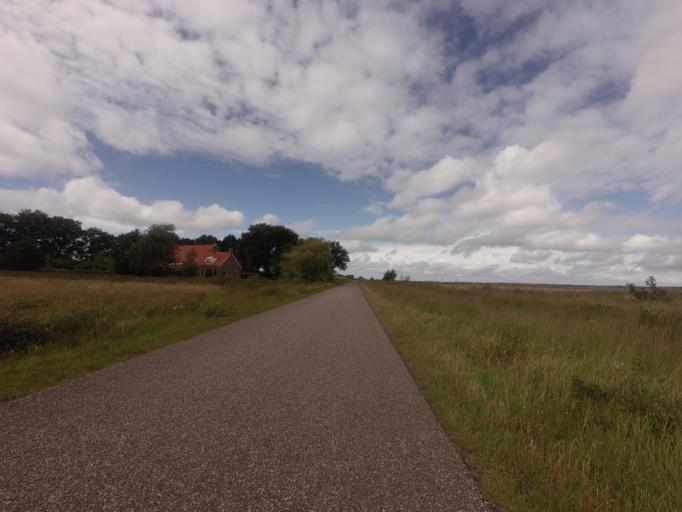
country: NL
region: Drenthe
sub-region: Gemeente Westerveld
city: Dwingeloo
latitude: 52.9956
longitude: 6.3782
